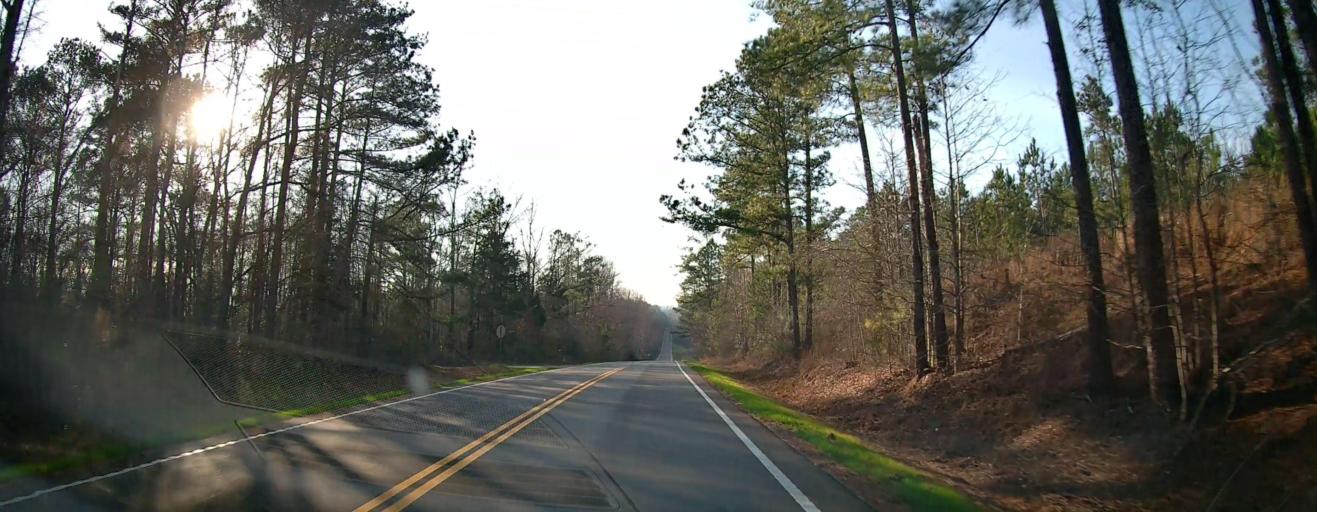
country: US
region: Georgia
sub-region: Harris County
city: Hamilton
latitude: 32.7480
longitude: -84.9145
